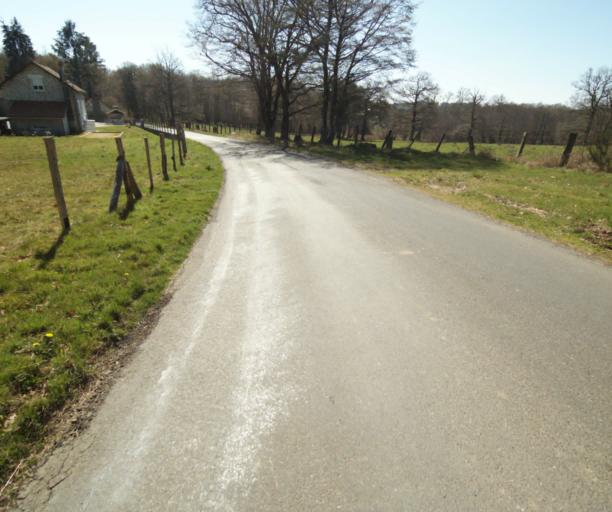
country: FR
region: Limousin
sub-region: Departement de la Correze
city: Saint-Clement
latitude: 45.3429
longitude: 1.6420
